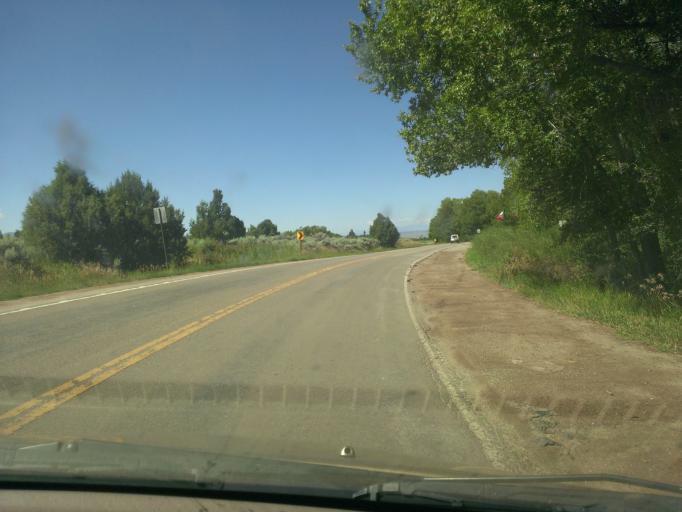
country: US
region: New Mexico
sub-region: Taos County
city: Arroyo Seco
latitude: 36.5152
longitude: -105.5710
